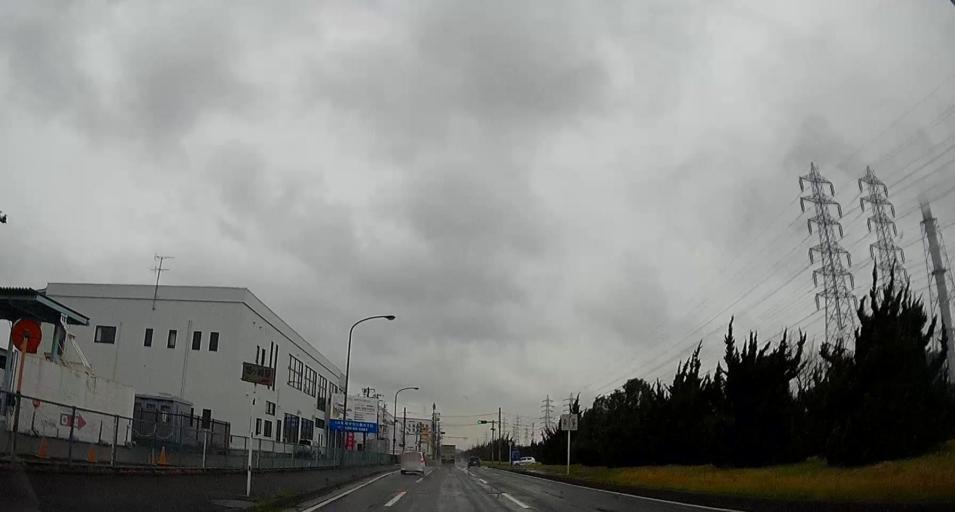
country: JP
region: Chiba
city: Ichihara
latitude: 35.4849
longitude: 140.0391
